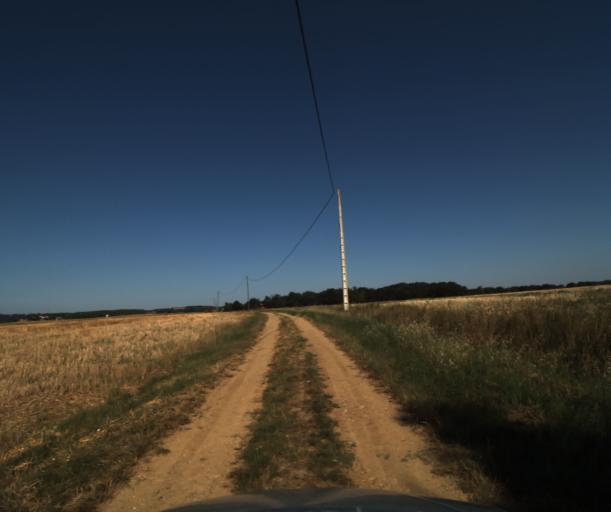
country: FR
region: Midi-Pyrenees
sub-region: Departement de la Haute-Garonne
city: Eaunes
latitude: 43.4277
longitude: 1.3700
